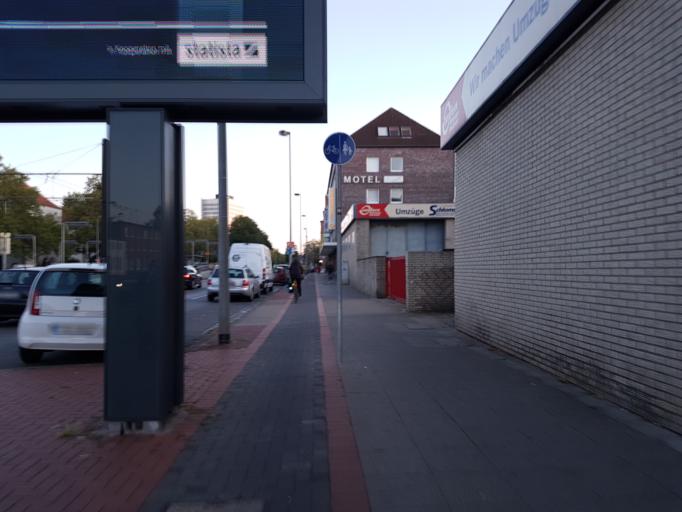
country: DE
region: Lower Saxony
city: Hannover
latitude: 52.4034
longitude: 9.7351
